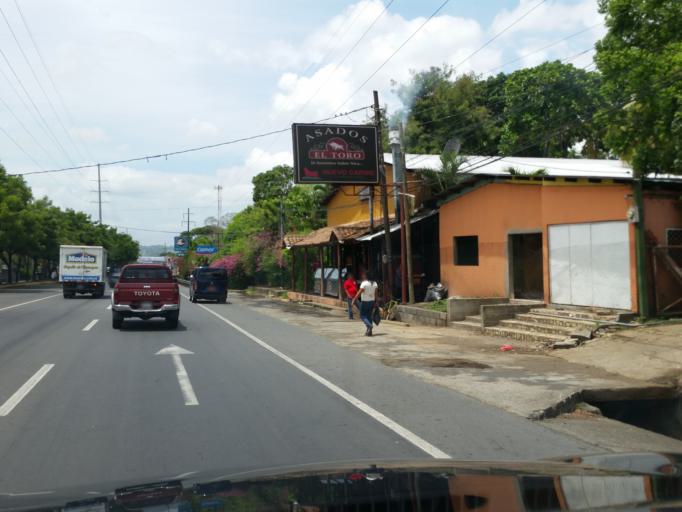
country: NI
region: Masaya
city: Ticuantepe
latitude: 12.0698
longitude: -86.2159
